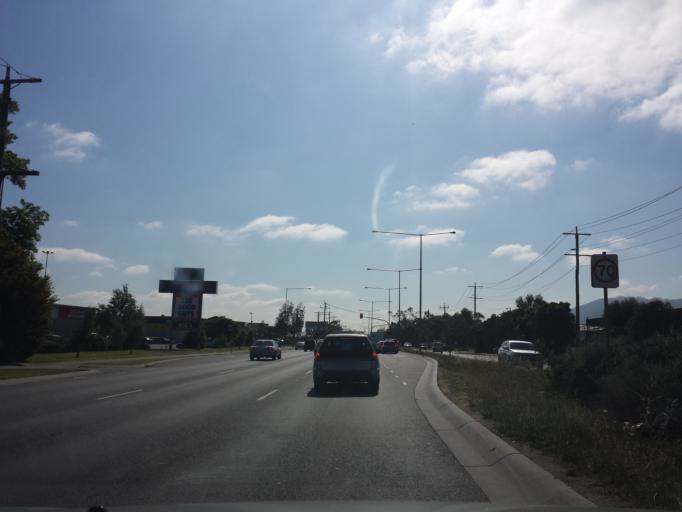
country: AU
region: Victoria
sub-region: Maroondah
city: Croydon South
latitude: -37.8293
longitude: 145.2778
